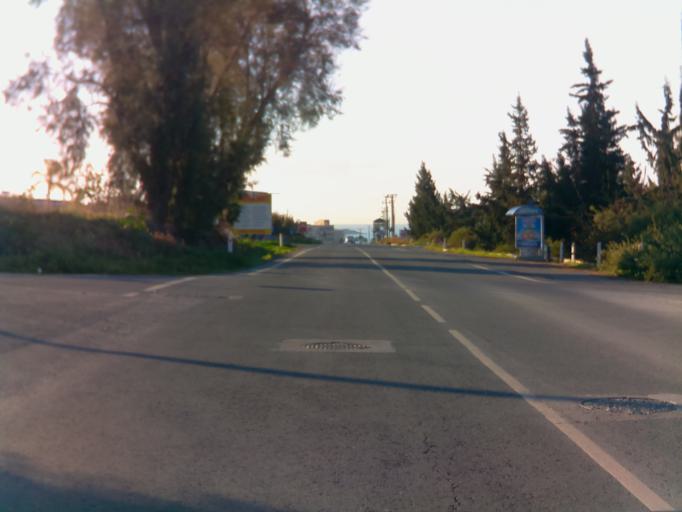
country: CY
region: Pafos
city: Kissonerga
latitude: 34.8275
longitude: 32.3923
